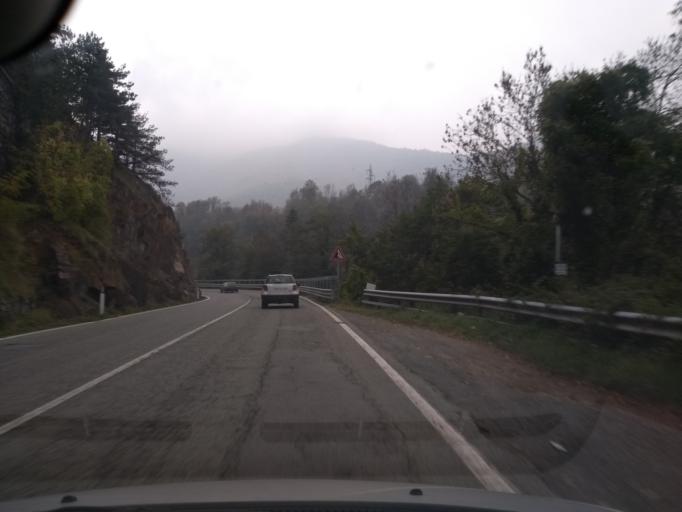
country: IT
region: Piedmont
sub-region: Provincia di Torino
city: Germagnano
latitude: 45.2648
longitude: 7.4574
